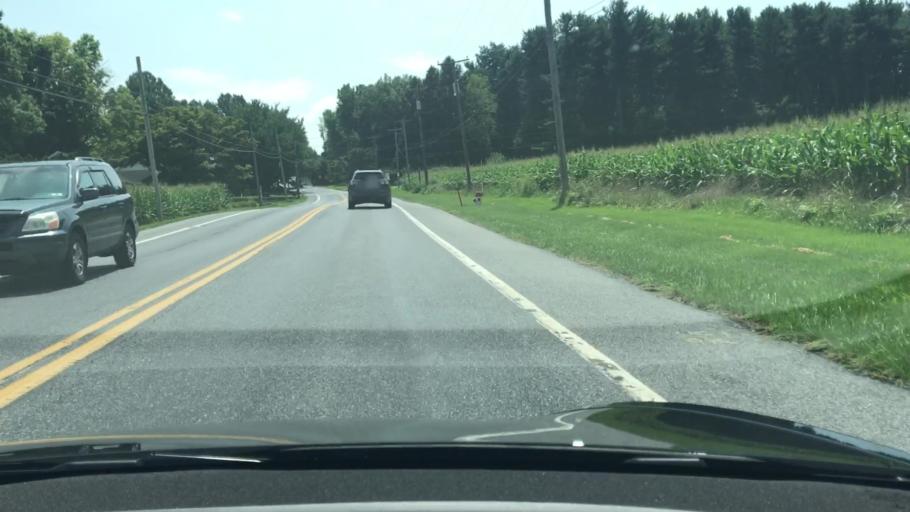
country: US
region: Pennsylvania
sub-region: Lancaster County
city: Landisville
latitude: 40.0826
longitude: -76.4087
